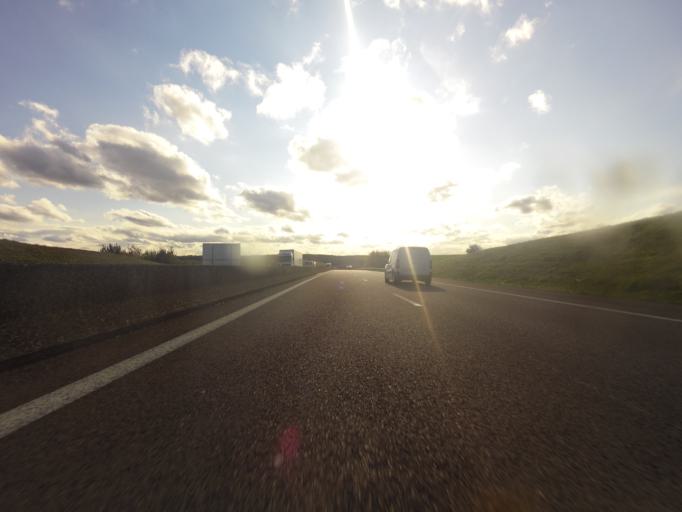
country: FR
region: Picardie
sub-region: Departement de la Somme
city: Saleux
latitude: 49.8535
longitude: 2.1597
